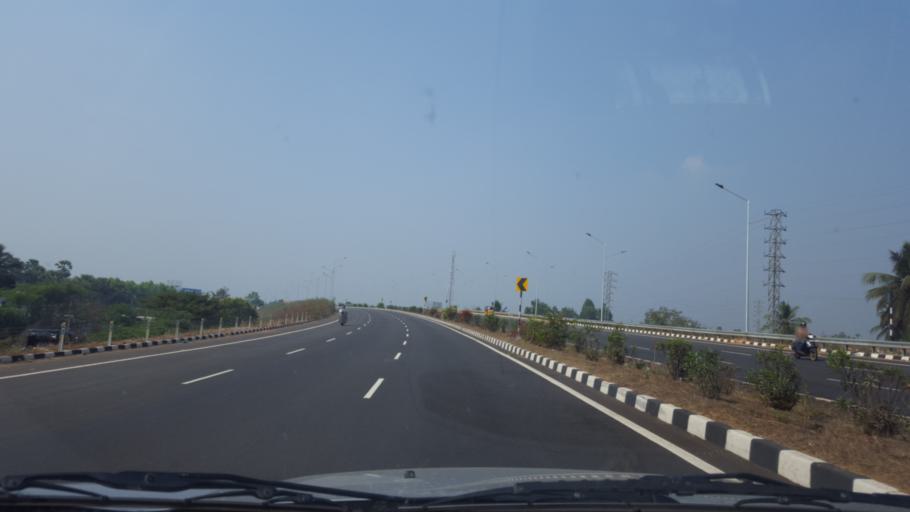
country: IN
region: Andhra Pradesh
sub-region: Vishakhapatnam
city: Bhimunipatnam
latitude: 17.9635
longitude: 83.4228
